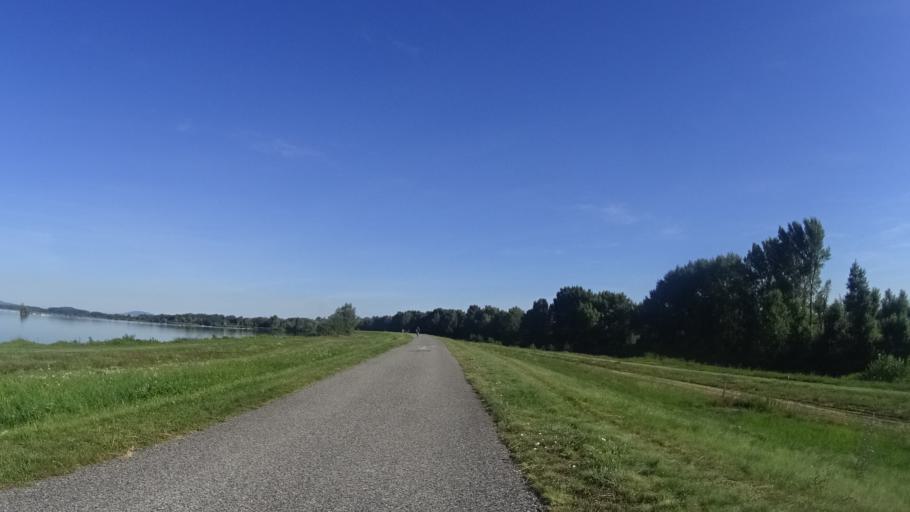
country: SK
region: Bratislavsky
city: Dunajska Luzna
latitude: 48.0480
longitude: 17.2385
